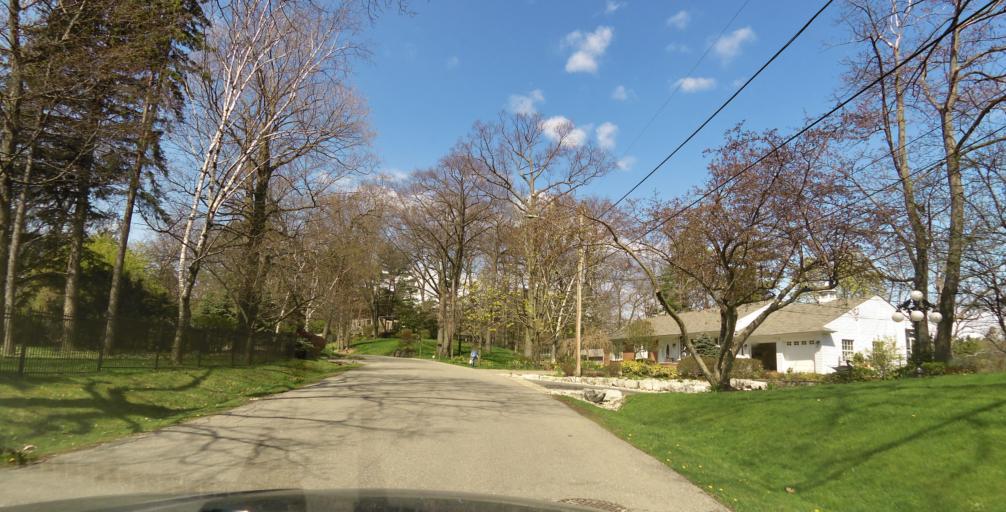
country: CA
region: Ontario
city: Mississauga
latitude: 43.5533
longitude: -79.6022
